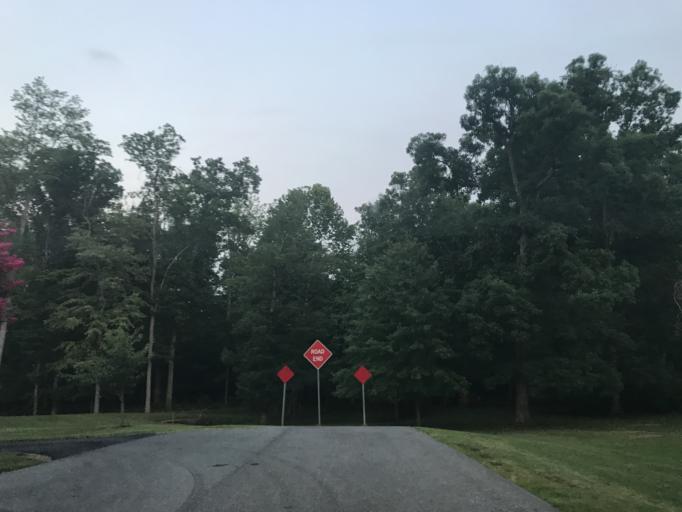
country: US
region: Maryland
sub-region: Baltimore County
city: White Marsh
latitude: 39.4110
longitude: -76.4261
